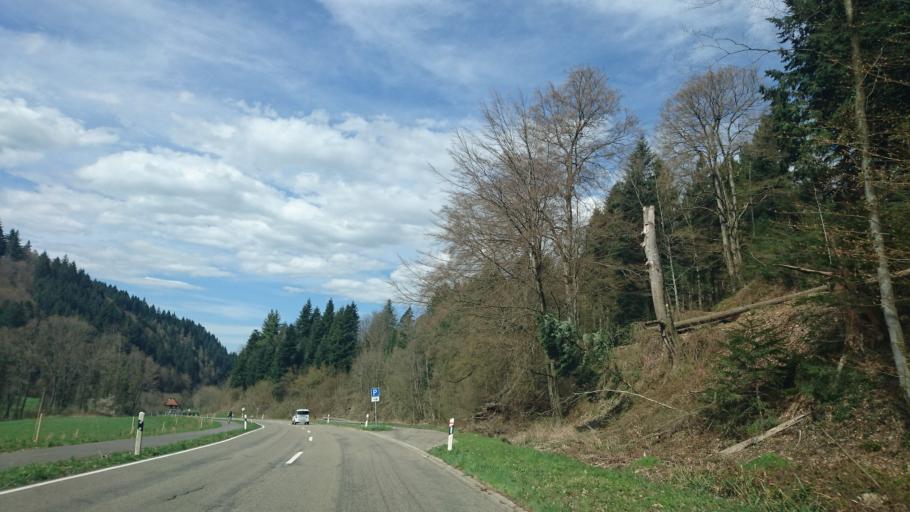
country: DE
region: Baden-Wuerttemberg
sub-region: Freiburg Region
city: Horben
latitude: 47.9472
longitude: 7.8672
